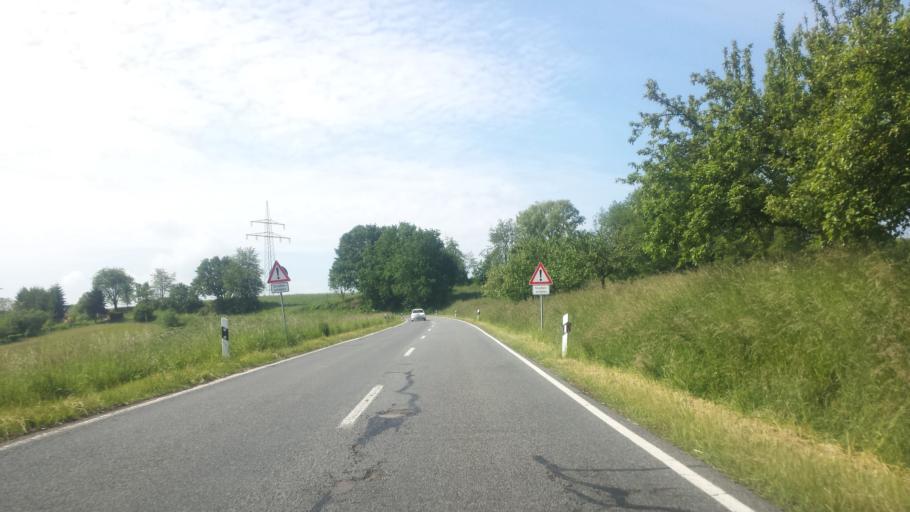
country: DE
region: Hesse
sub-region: Regierungsbezirk Darmstadt
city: Rimbach
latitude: 49.6051
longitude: 8.7573
